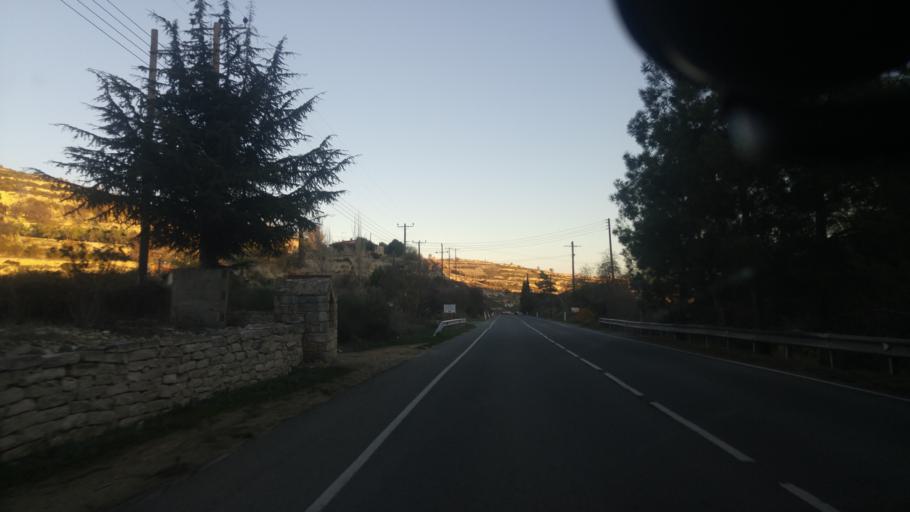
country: CY
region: Limassol
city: Pachna
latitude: 34.7954
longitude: 32.8172
